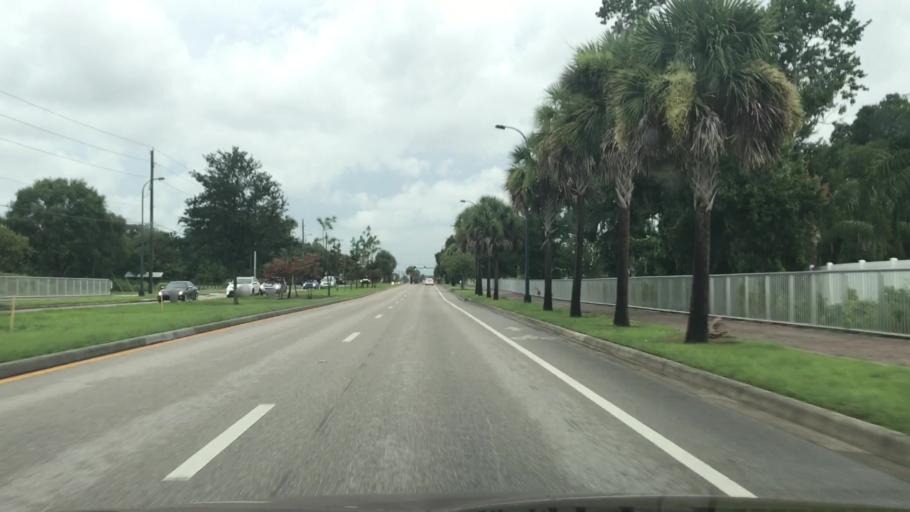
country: US
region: Florida
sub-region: Sarasota County
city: Fruitville
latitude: 27.3384
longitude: -82.4240
